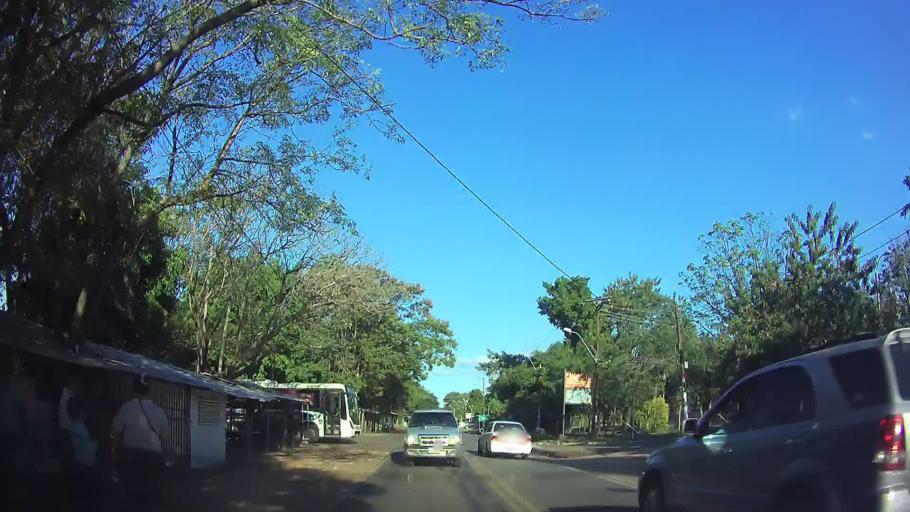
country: PY
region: Central
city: Aregua
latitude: -25.3116
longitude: -57.3790
